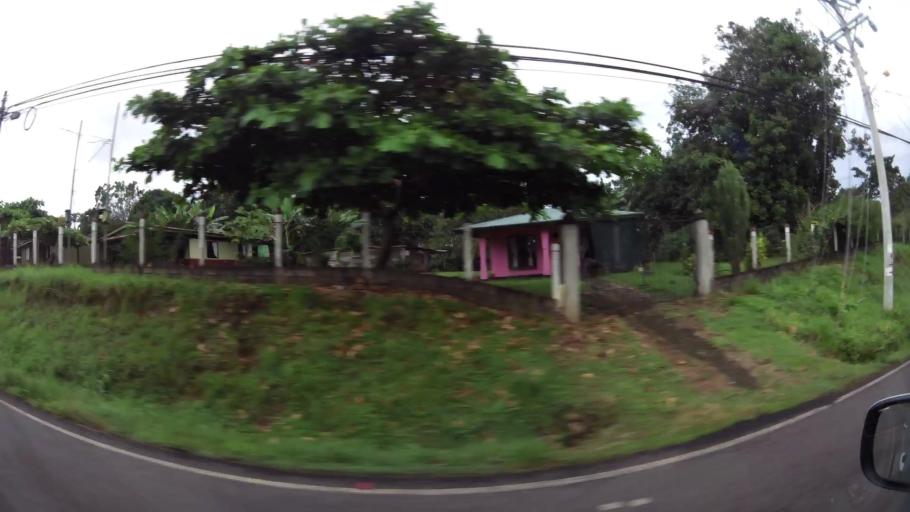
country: CR
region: Puntarenas
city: Esparza
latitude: 9.9630
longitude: -84.6135
